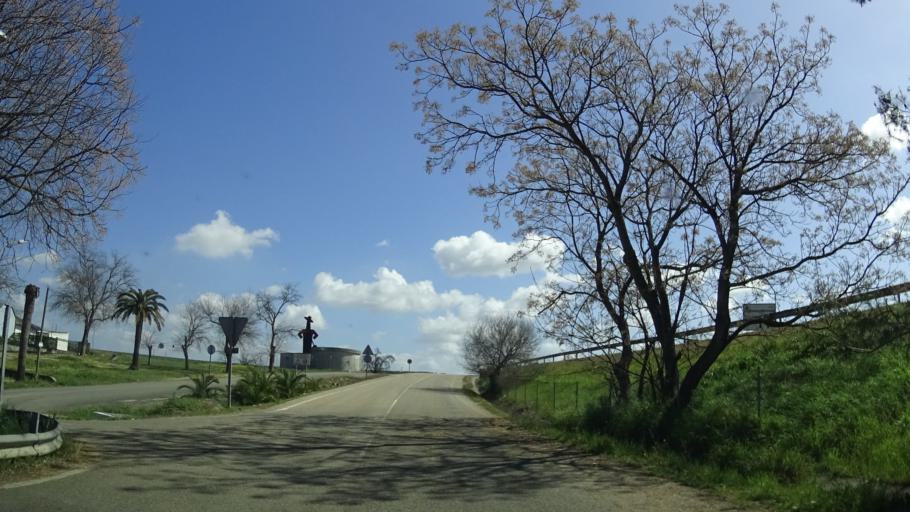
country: ES
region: Andalusia
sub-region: Province of Cordoba
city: Montoro
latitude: 38.0056
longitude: -4.3483
